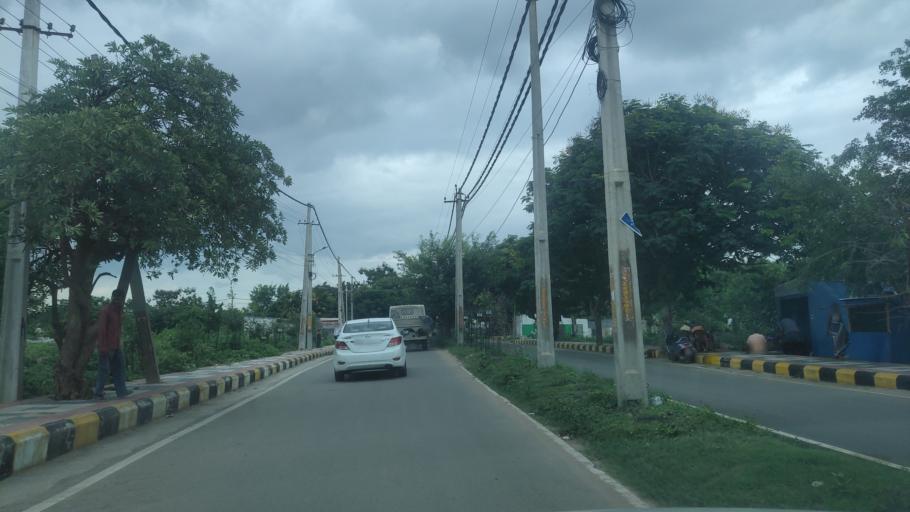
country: IN
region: Telangana
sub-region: Medak
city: Serilingampalle
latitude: 17.5019
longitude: 78.3514
